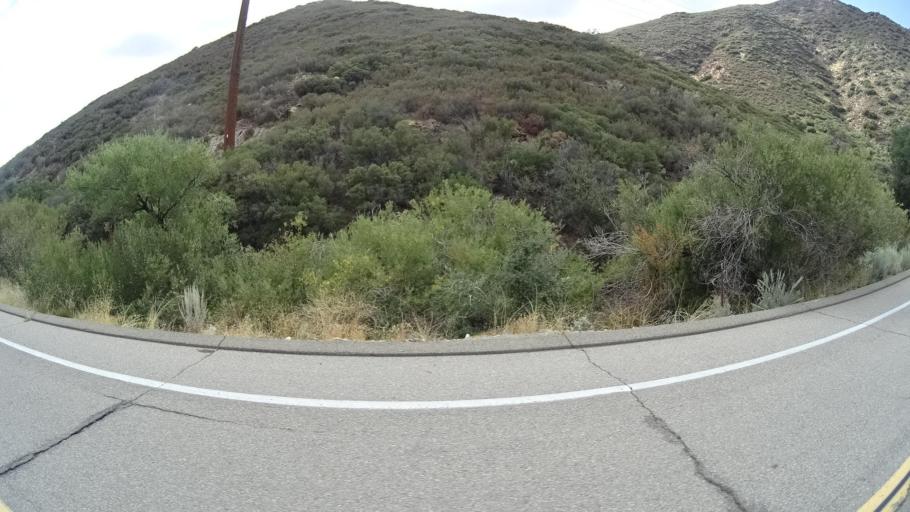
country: US
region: California
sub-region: San Diego County
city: Pine Valley
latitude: 32.7868
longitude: -116.4959
